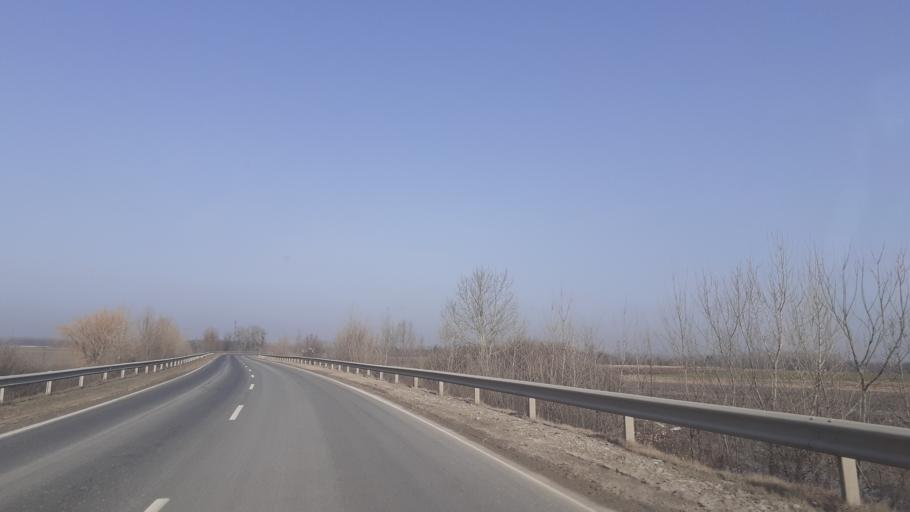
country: HU
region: Pest
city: Bugyi
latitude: 47.2372
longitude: 19.1208
